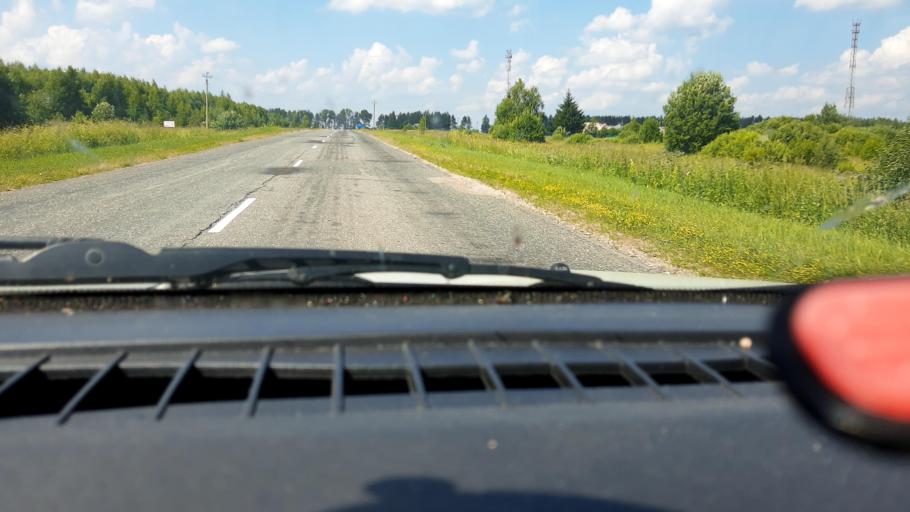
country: RU
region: Nizjnij Novgorod
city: Tonkino
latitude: 57.3671
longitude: 46.4228
